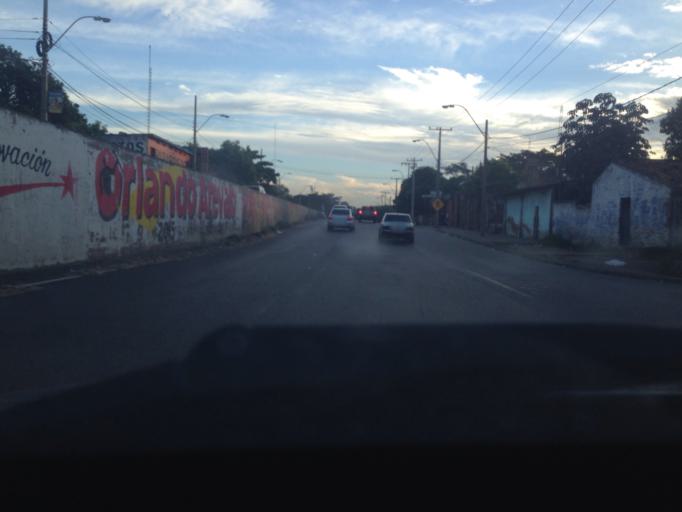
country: PY
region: Central
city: Lambare
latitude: -25.3413
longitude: -57.5861
